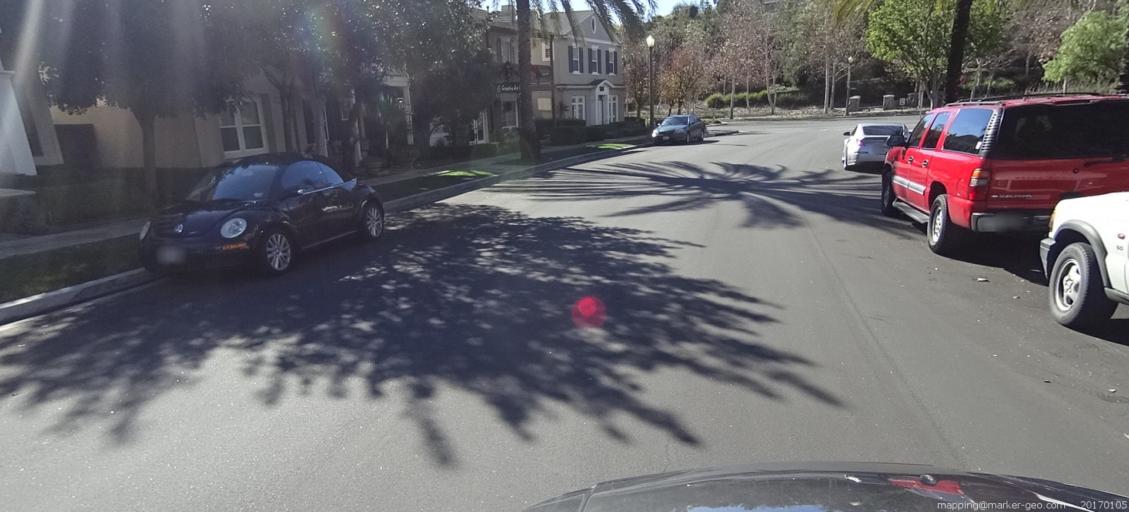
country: US
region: California
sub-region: Orange County
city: Ladera Ranch
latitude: 33.5503
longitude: -117.6375
